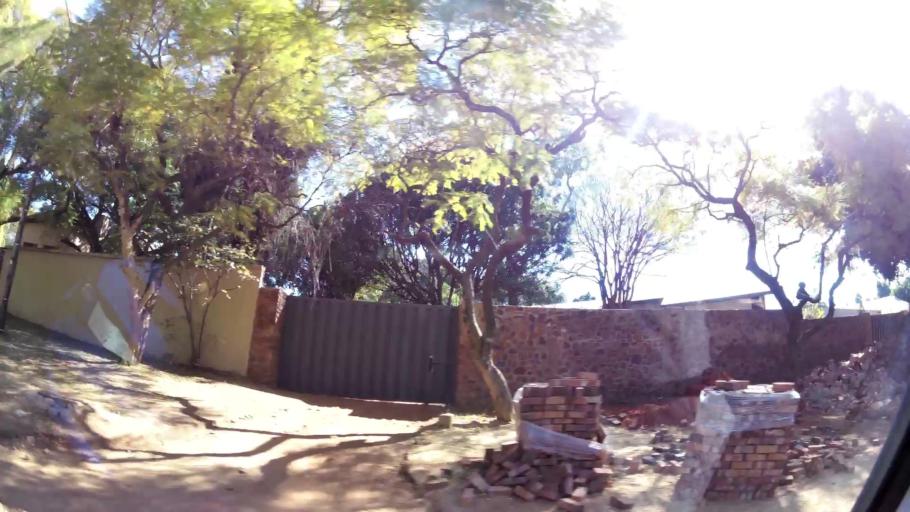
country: ZA
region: Gauteng
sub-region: City of Tshwane Metropolitan Municipality
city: Pretoria
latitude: -25.7897
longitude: 28.2414
